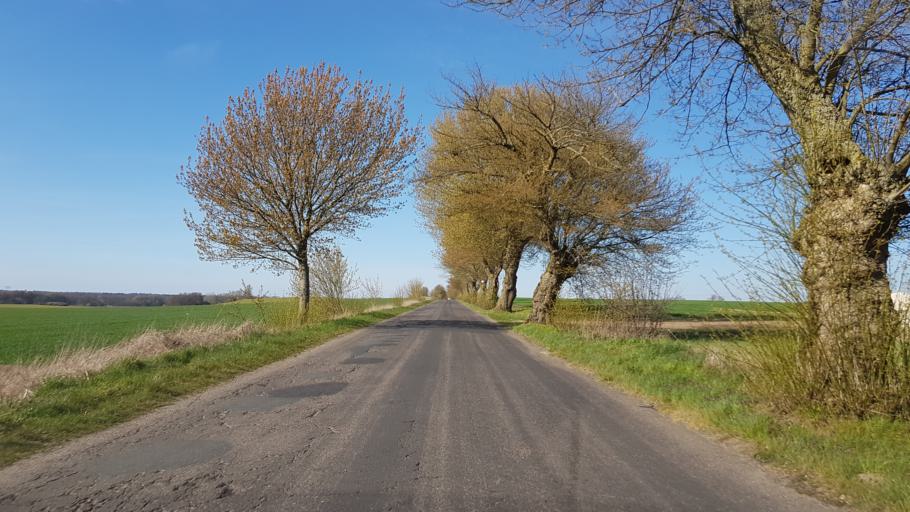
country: PL
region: West Pomeranian Voivodeship
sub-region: Powiat stargardzki
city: Stargard Szczecinski
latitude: 53.3793
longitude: 15.0335
